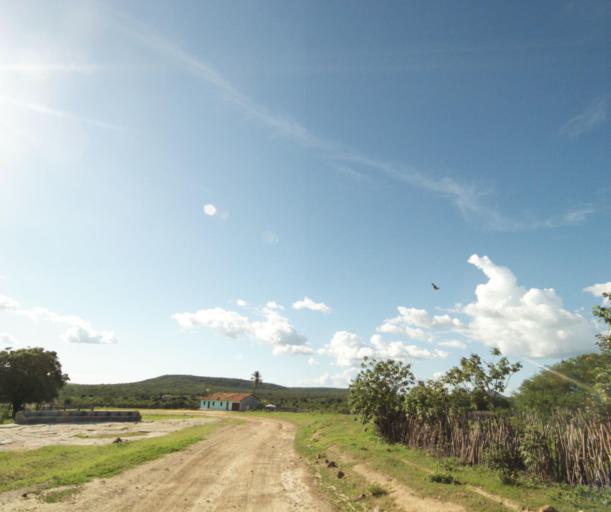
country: BR
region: Bahia
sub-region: Tanhacu
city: Tanhacu
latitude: -14.1869
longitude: -40.9469
